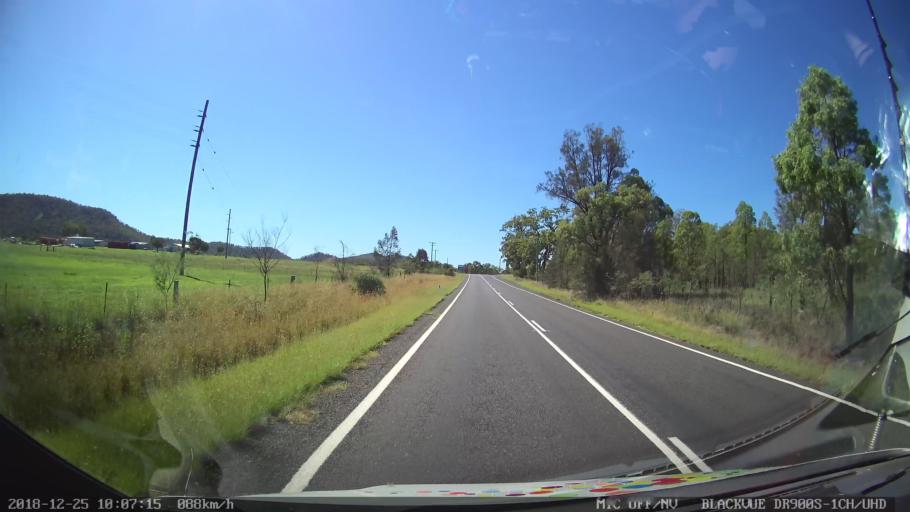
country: AU
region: New South Wales
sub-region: Upper Hunter Shire
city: Merriwa
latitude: -32.2688
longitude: 150.4968
